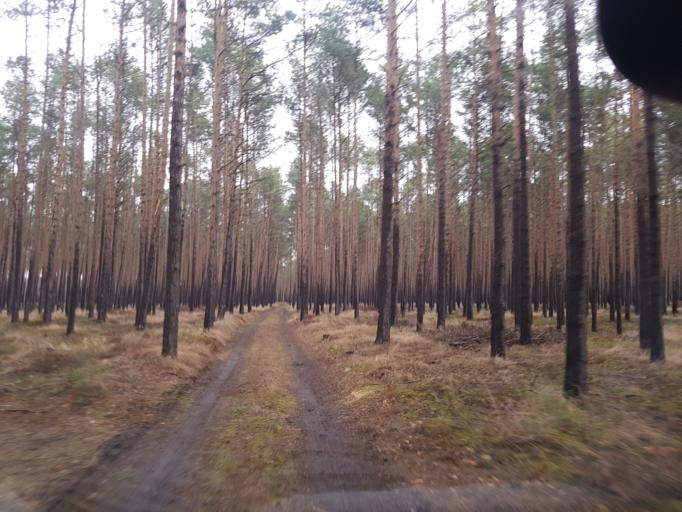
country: DE
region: Brandenburg
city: Finsterwalde
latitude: 51.5727
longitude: 13.6866
